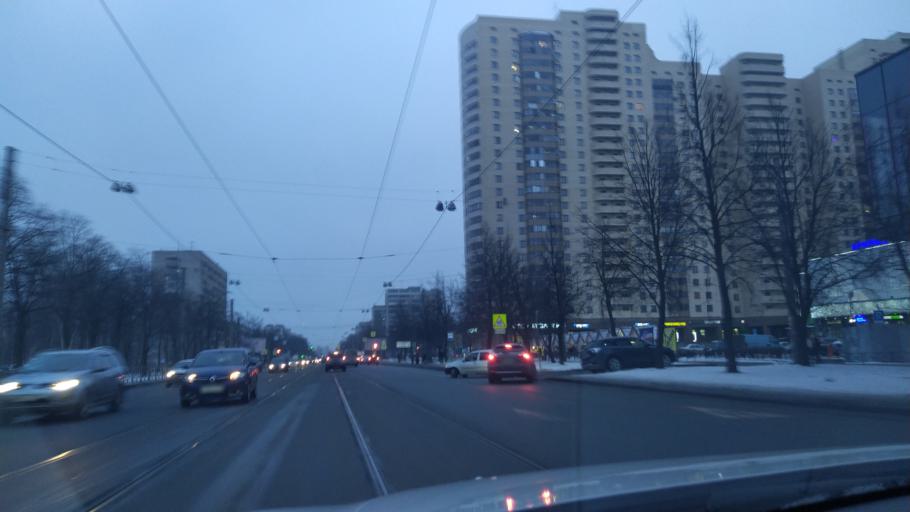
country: RU
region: Leningrad
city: Akademicheskoe
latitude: 60.0117
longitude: 30.4031
